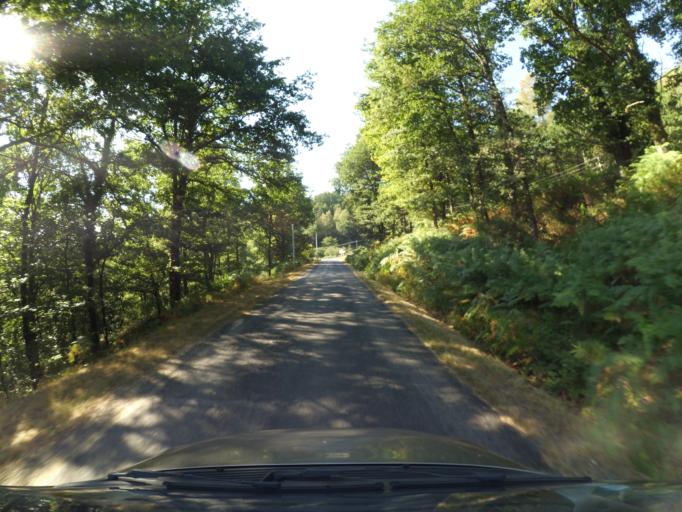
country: FR
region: Limousin
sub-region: Departement de la Haute-Vienne
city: Peyrat-le-Chateau
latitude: 45.7571
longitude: 1.8147
